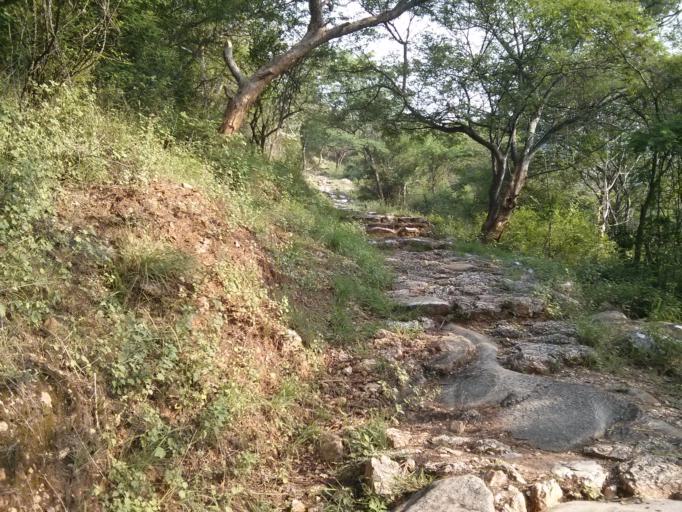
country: IN
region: Tamil Nadu
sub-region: Coimbatore
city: Periyanayakkanpalaiyam
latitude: 11.1504
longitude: 76.8870
